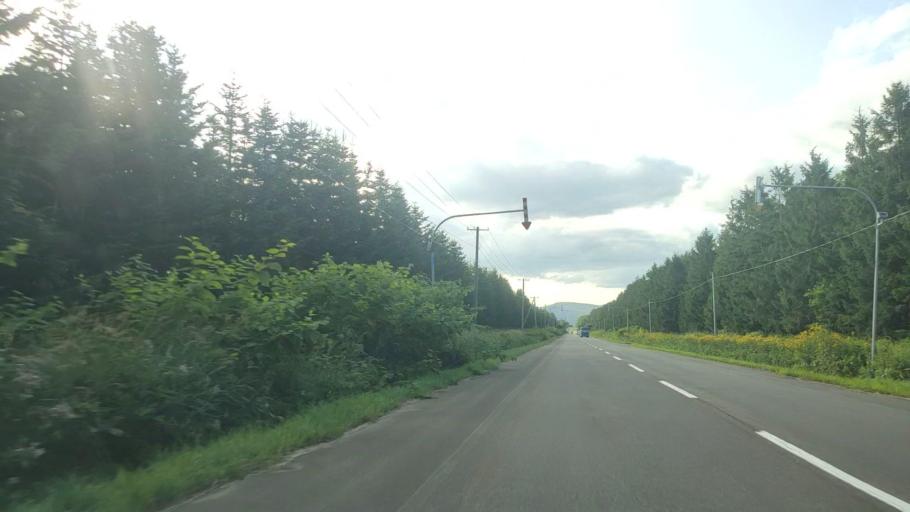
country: JP
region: Hokkaido
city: Makubetsu
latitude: 44.8873
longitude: 142.0074
